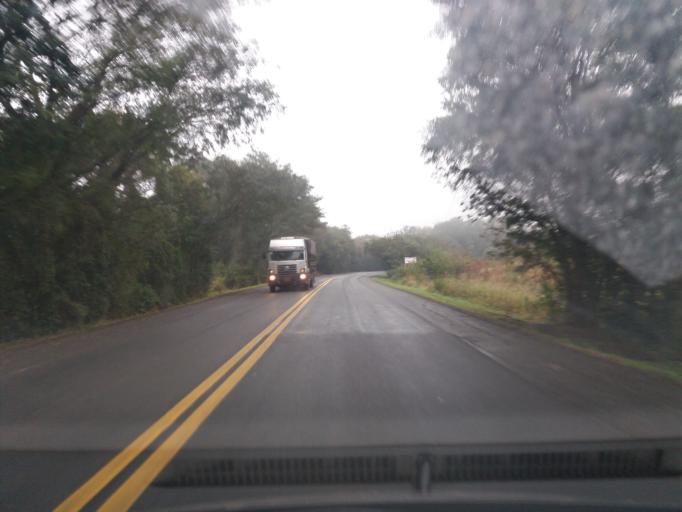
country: BR
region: Parana
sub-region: Ampere
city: Ampere
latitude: -25.8756
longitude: -53.4806
